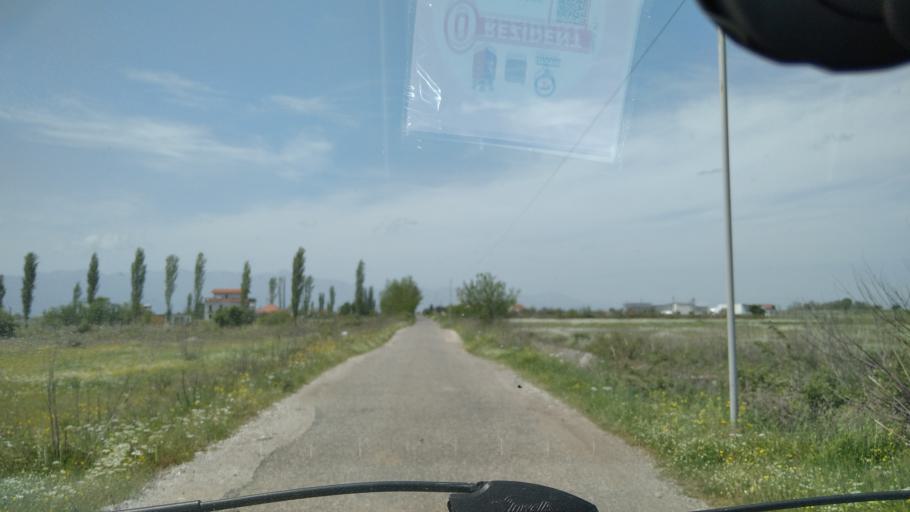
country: AL
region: Shkoder
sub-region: Rrethi i Malesia e Madhe
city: Gruemire
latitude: 42.1425
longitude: 19.5114
